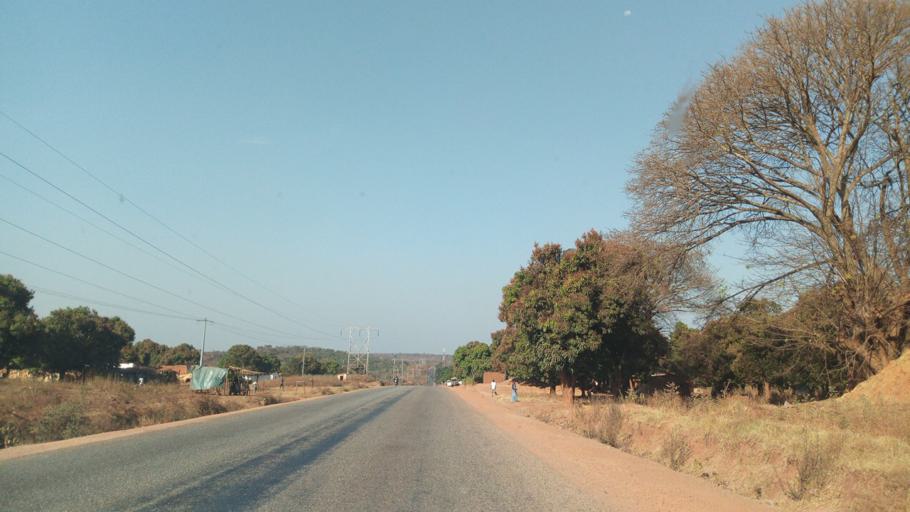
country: CD
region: Katanga
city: Likasi
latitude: -11.0008
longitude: 26.8797
